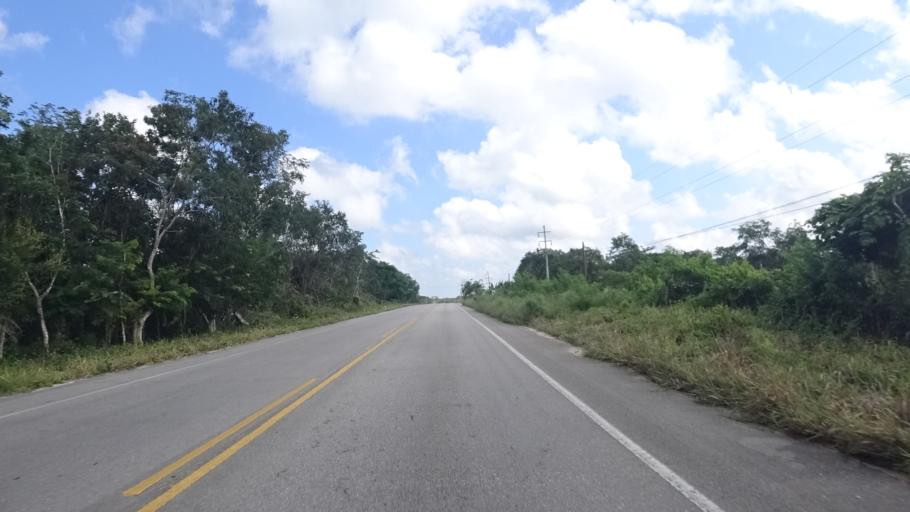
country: MX
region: Yucatan
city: Espita
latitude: 20.9904
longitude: -88.1757
